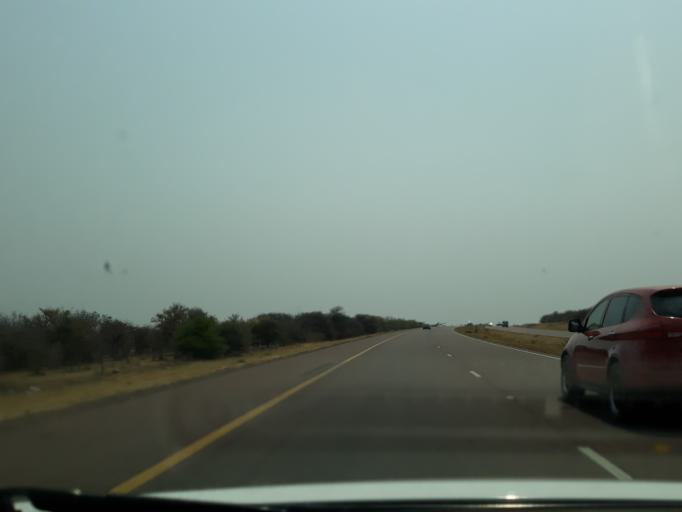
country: BW
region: Kgatleng
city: Bokaa
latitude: -24.4210
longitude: 26.0475
